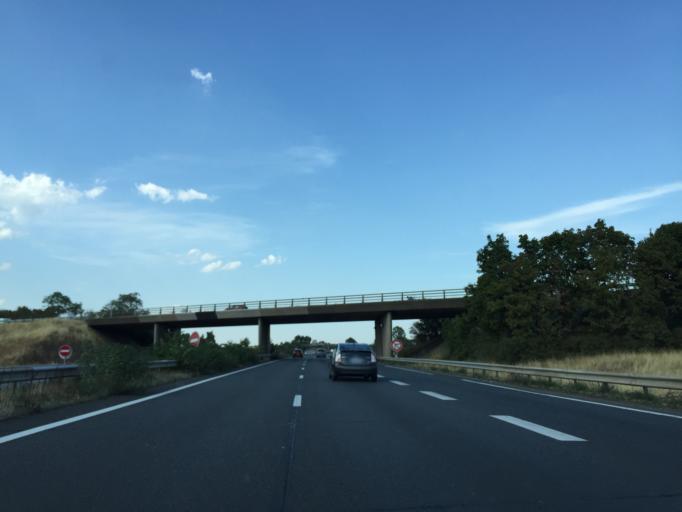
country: FR
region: Alsace
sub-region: Departement du Bas-Rhin
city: Chatenois
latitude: 48.2631
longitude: 7.4191
